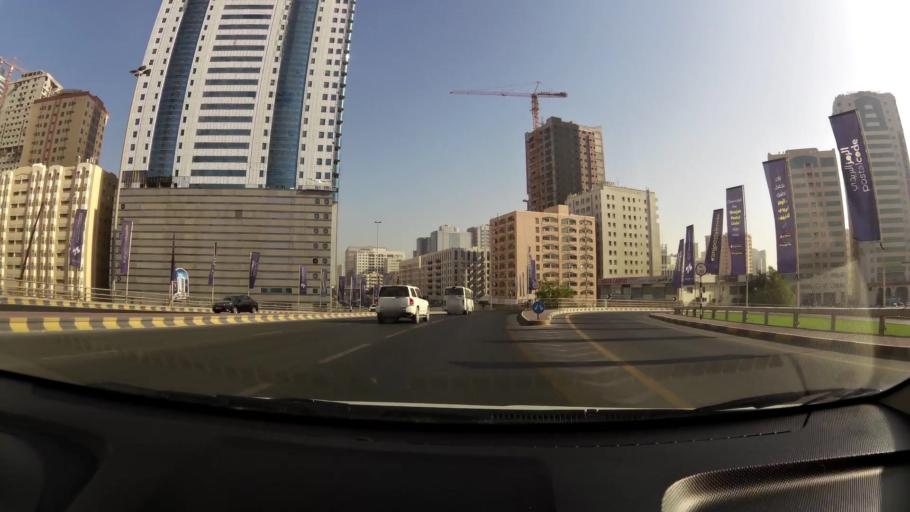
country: AE
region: Ash Shariqah
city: Sharjah
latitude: 25.3289
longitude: 55.3949
